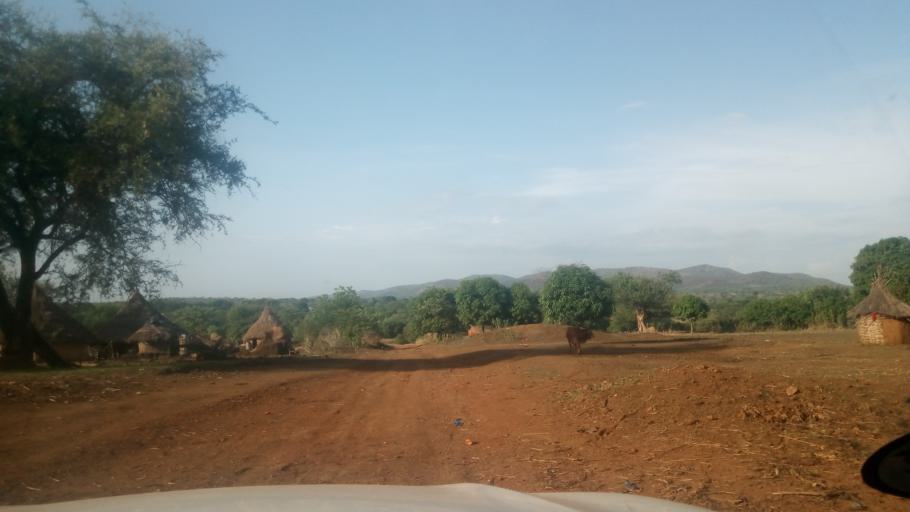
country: ET
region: Oromiya
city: Mendi
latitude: 10.2089
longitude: 35.0783
